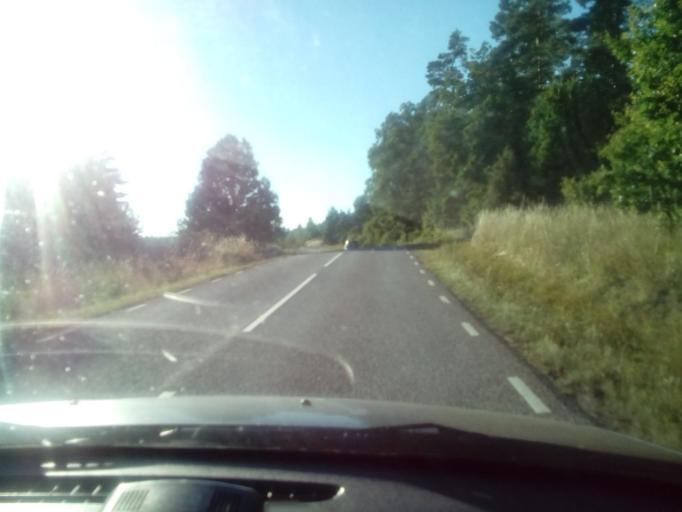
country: SE
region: Kalmar
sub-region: Vasterviks Kommun
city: Gamleby
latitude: 57.7941
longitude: 16.3738
